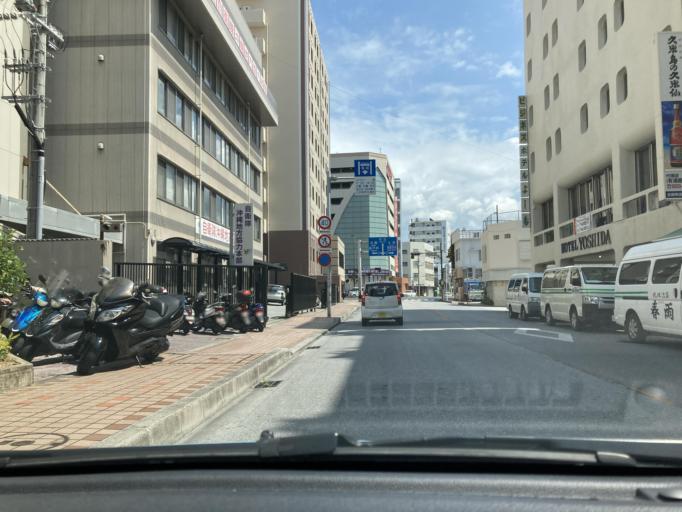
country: JP
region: Okinawa
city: Naha-shi
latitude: 26.2232
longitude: 127.6830
